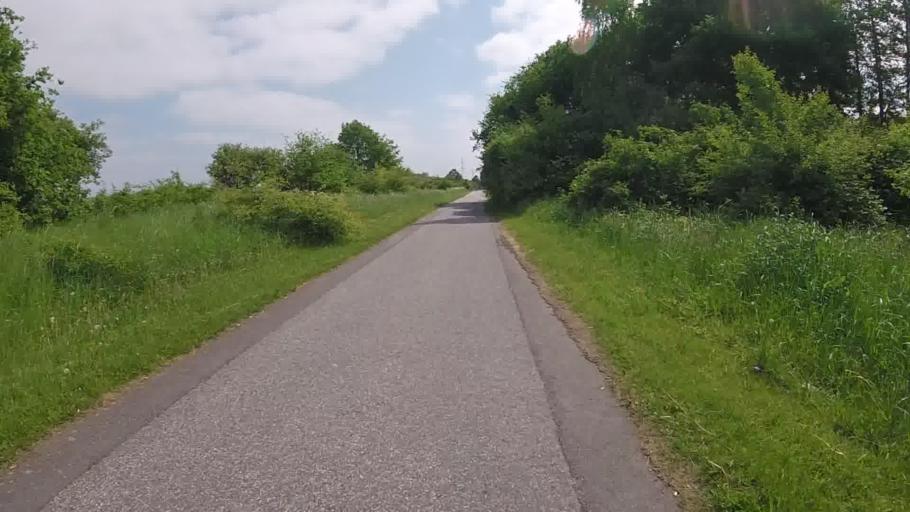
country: DE
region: Schleswig-Holstein
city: Oststeinbek
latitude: 53.4906
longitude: 10.1601
